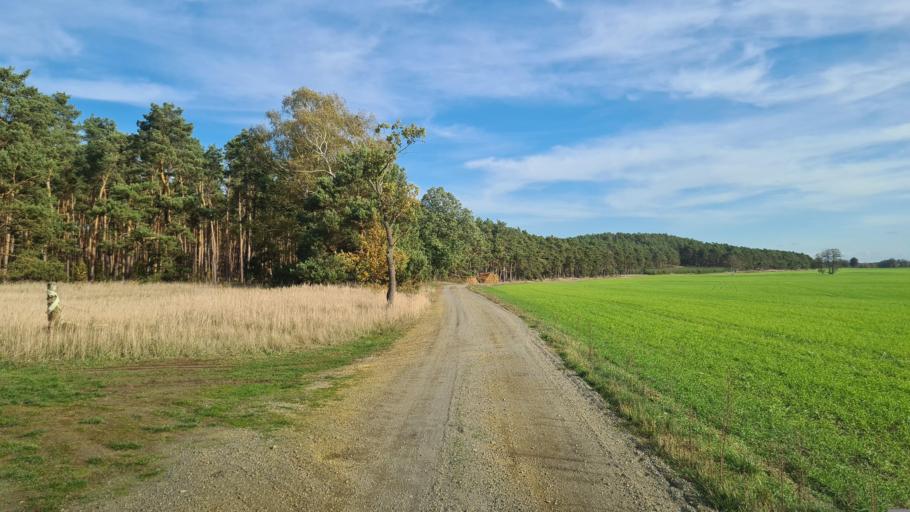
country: DE
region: Brandenburg
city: Schlieben
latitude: 51.7373
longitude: 13.4089
